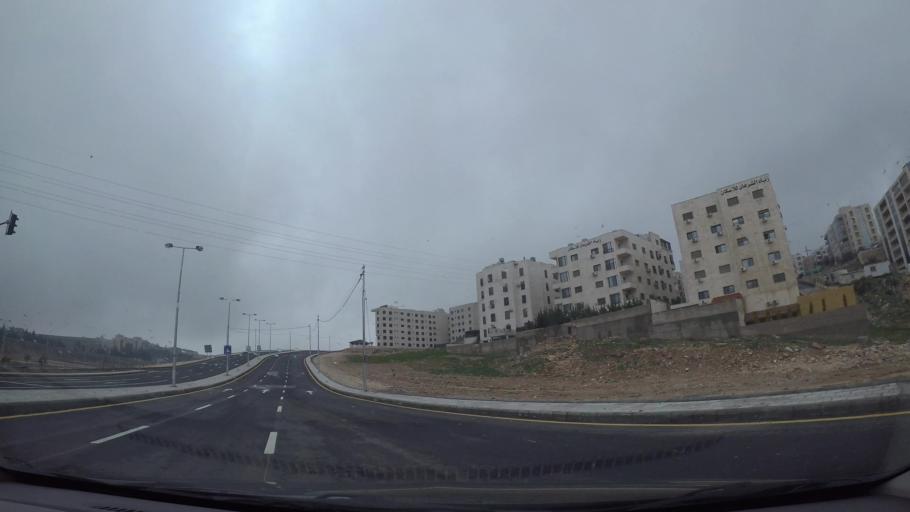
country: JO
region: Amman
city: Wadi as Sir
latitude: 31.9338
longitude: 35.8618
